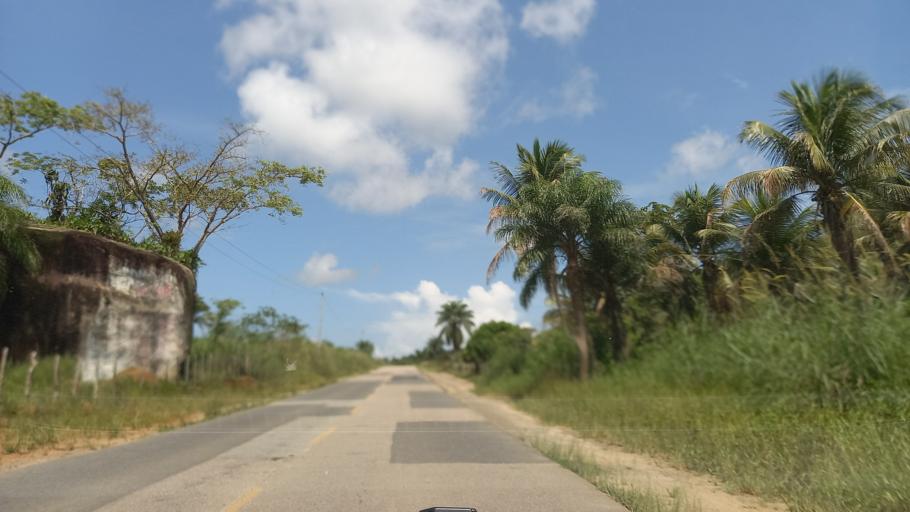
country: BR
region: Pernambuco
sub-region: Barreiros
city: Barreiros
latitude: -8.7608
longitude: -35.1709
